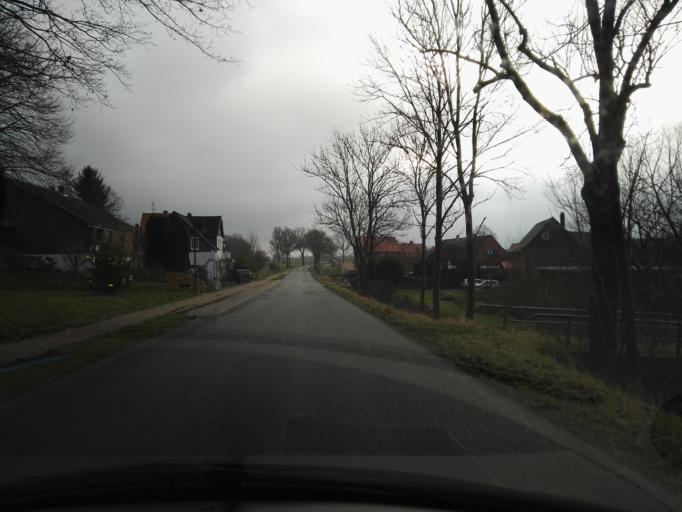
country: DE
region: Lower Saxony
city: Eberholzen
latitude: 52.0758
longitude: 9.8675
